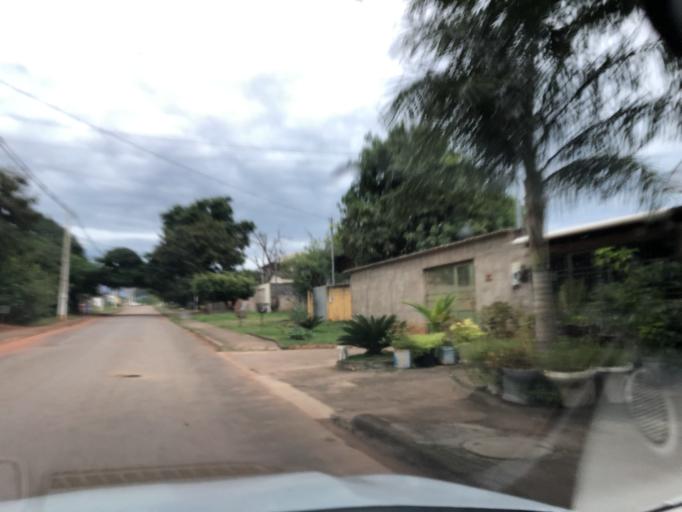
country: BR
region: Goias
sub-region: Luziania
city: Luziania
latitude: -16.1090
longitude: -47.9740
